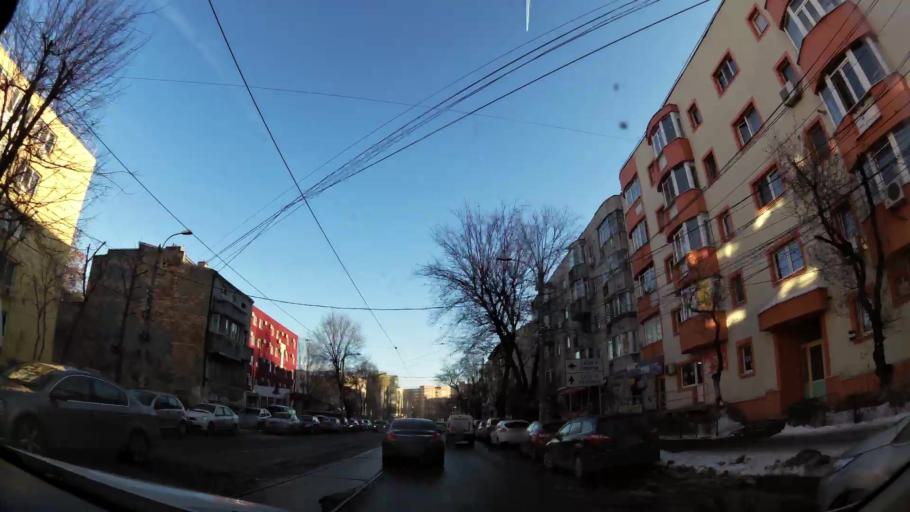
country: RO
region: Bucuresti
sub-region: Municipiul Bucuresti
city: Bucharest
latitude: 44.4472
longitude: 26.1332
